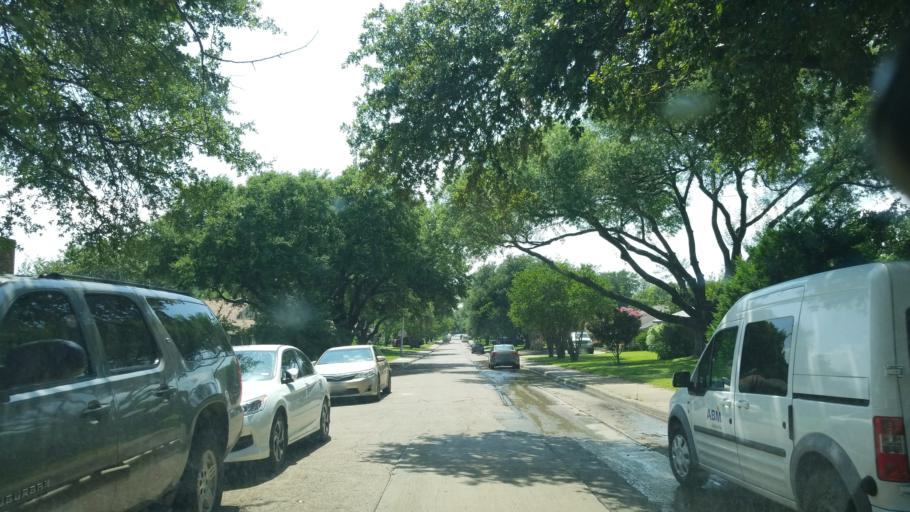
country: US
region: Texas
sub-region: Dallas County
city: Farmers Branch
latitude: 32.8773
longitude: -96.8726
